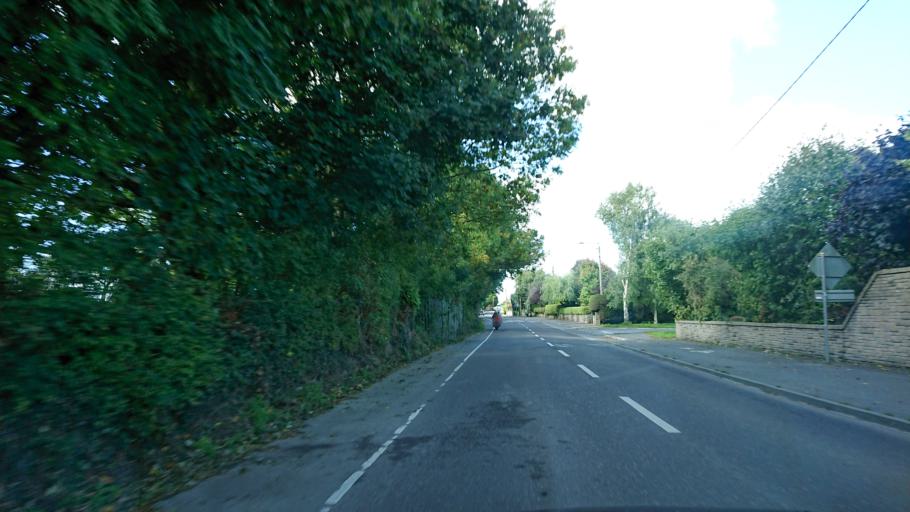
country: IE
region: Munster
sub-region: Waterford
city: Dungarvan
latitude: 52.0932
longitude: -7.6369
